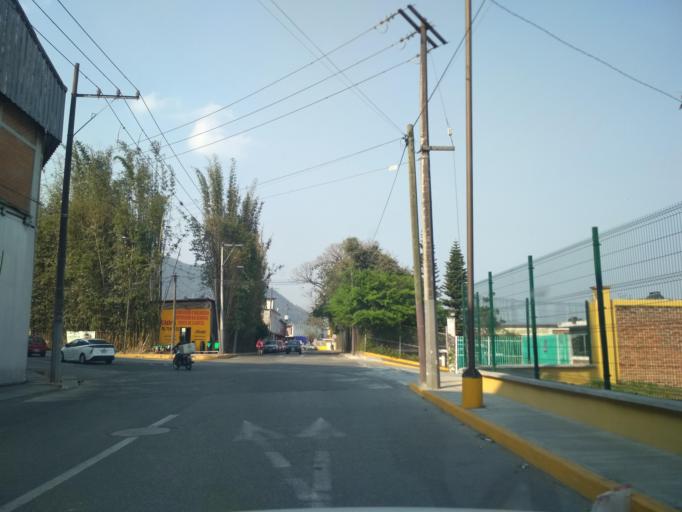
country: MX
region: Veracruz
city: Orizaba
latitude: 18.8455
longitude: -97.0871
